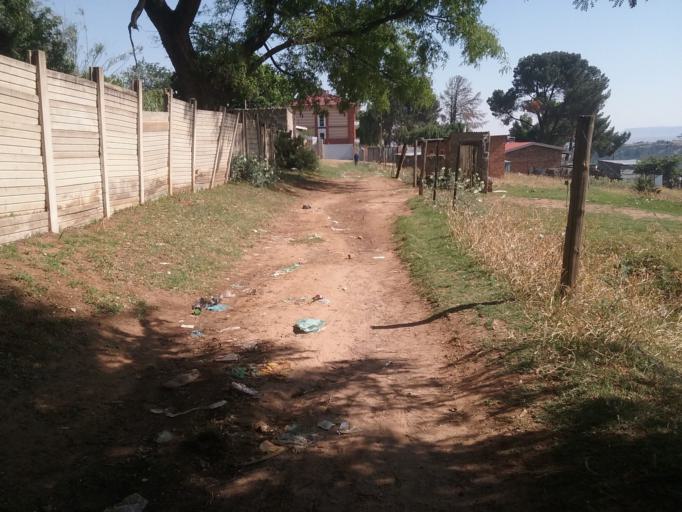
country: LS
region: Berea
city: Teyateyaneng
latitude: -29.1490
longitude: 27.7426
